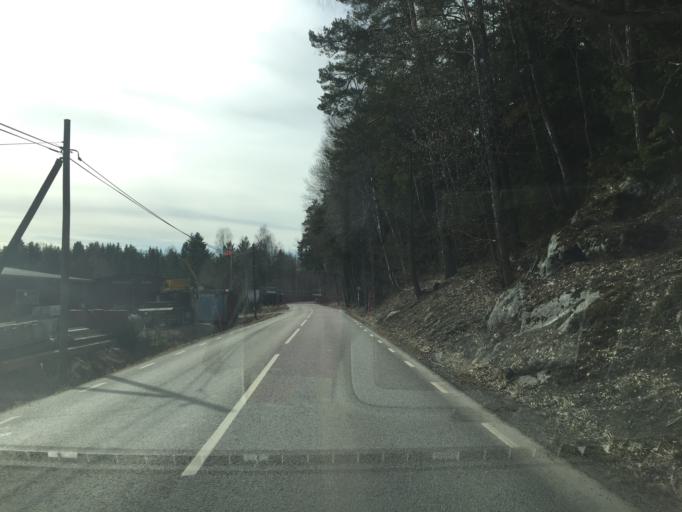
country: SE
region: Stockholm
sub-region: Botkyrka Kommun
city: Tullinge
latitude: 59.1088
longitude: 17.9890
